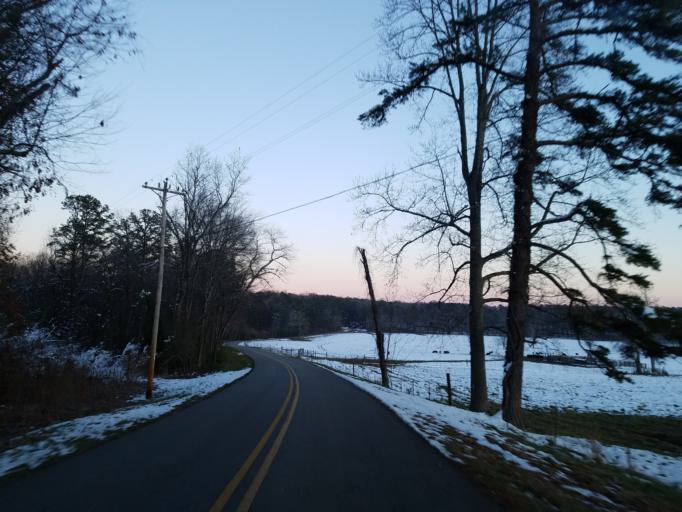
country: US
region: Georgia
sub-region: Pickens County
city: Nelson
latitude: 34.4006
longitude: -84.3797
